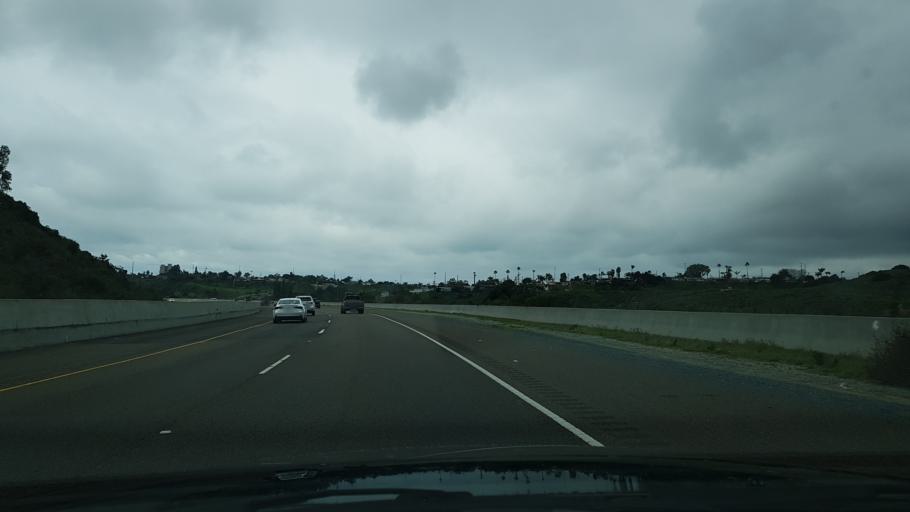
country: US
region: California
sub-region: San Diego County
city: Camp Pendleton South
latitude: 33.2127
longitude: -117.3727
